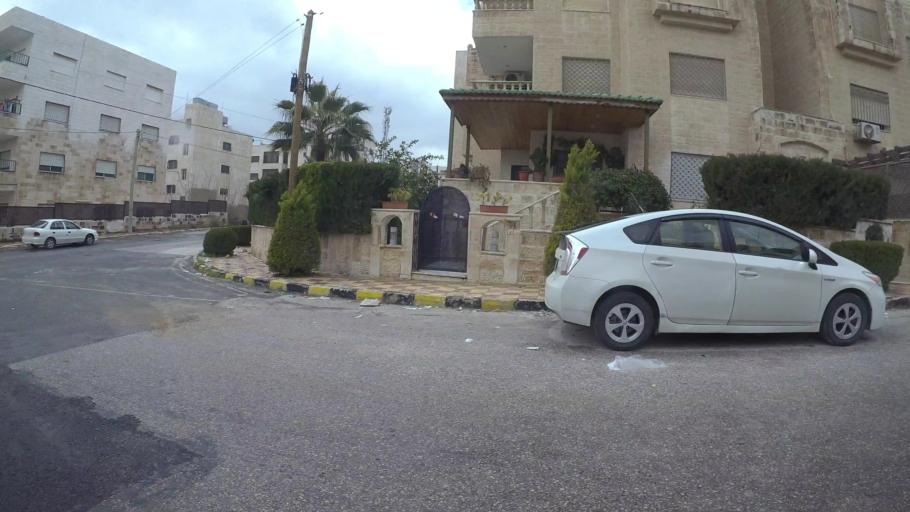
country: JO
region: Amman
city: Al Jubayhah
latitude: 31.9912
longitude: 35.8576
